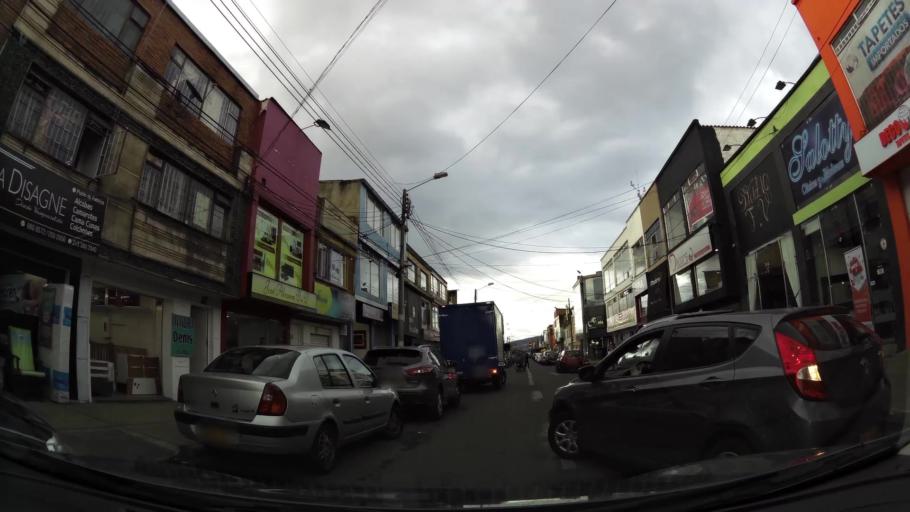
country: CO
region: Bogota D.C.
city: Barrio San Luis
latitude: 4.6702
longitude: -74.0732
